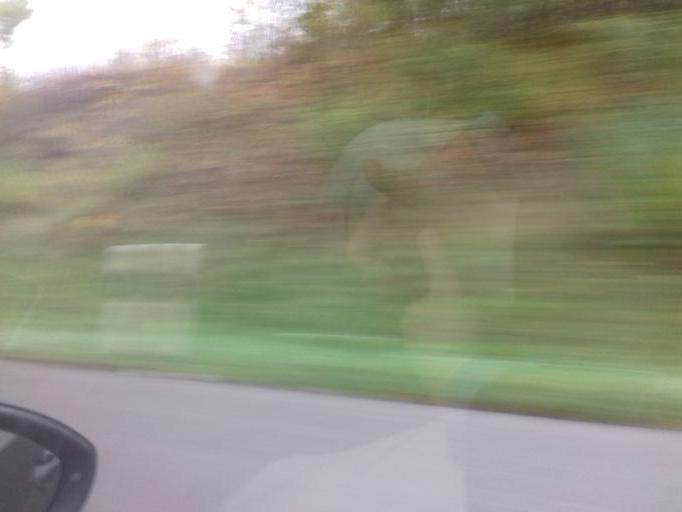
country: LU
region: Luxembourg
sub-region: Canton de Luxembourg
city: Niederanven
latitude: 49.6431
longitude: 6.2916
